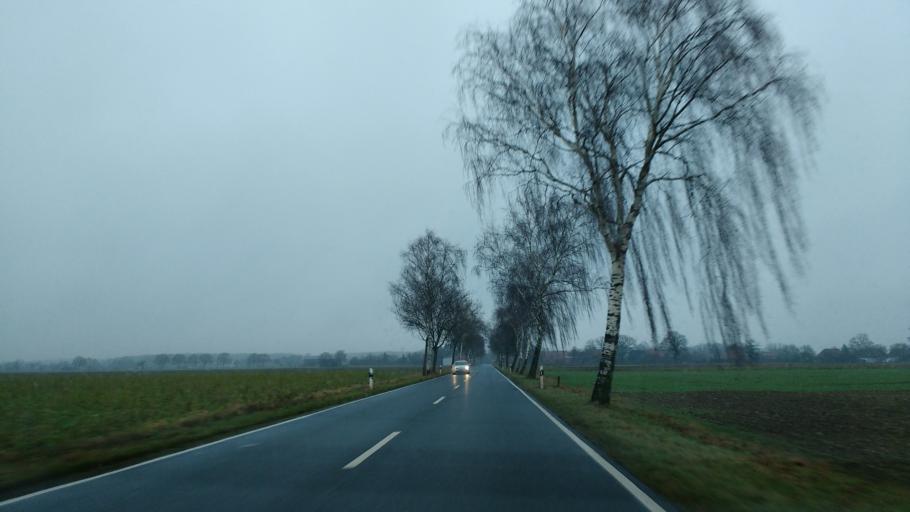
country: DE
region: Lower Saxony
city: Gilten
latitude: 52.6579
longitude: 9.5738
